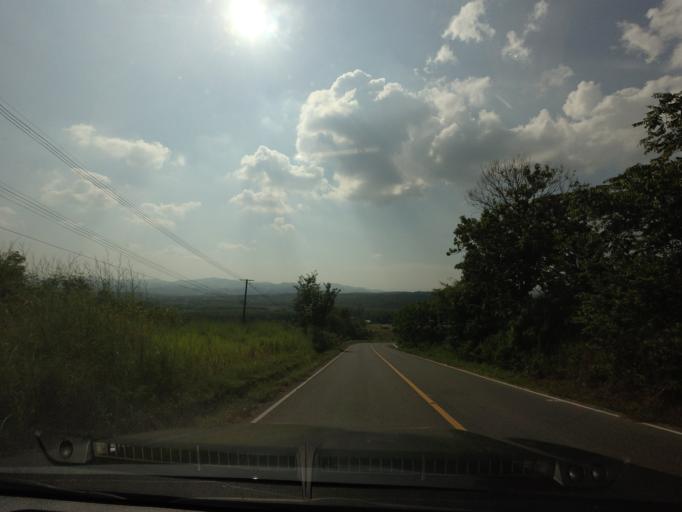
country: TH
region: Nan
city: Santi Suk
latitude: 18.9823
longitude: 100.9440
